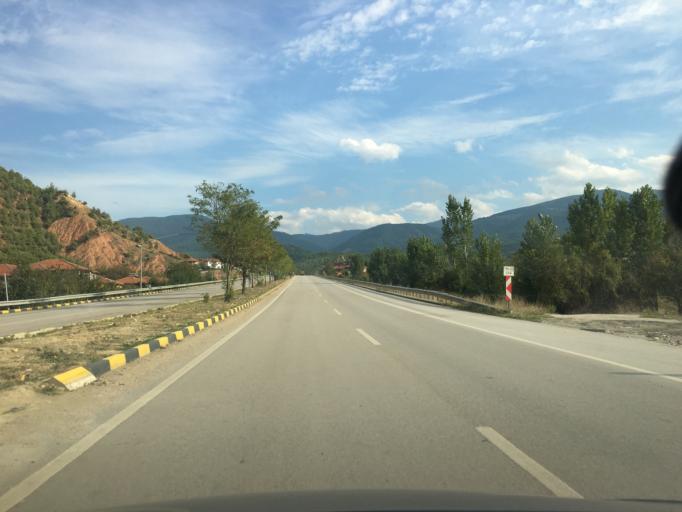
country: TR
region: Karabuk
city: Karabuk
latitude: 41.0993
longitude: 32.6722
